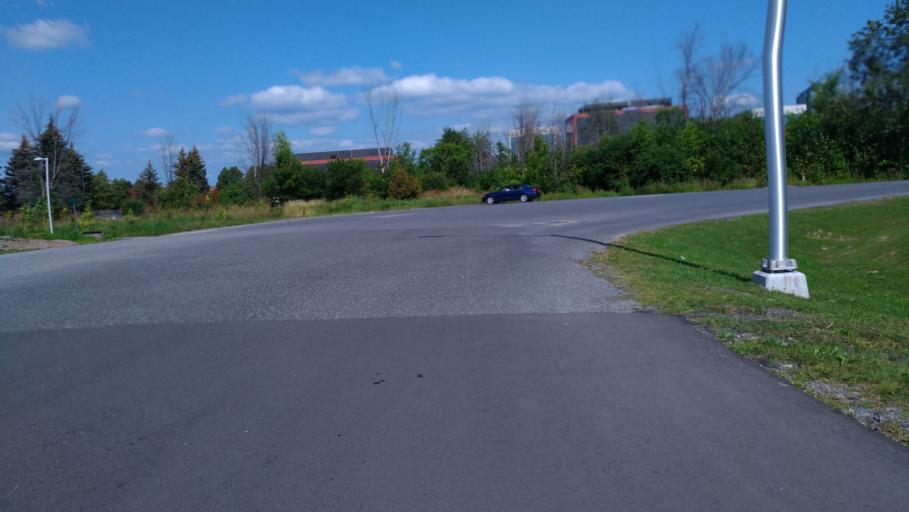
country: CA
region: Ontario
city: Bells Corners
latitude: 45.3462
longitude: -75.9258
